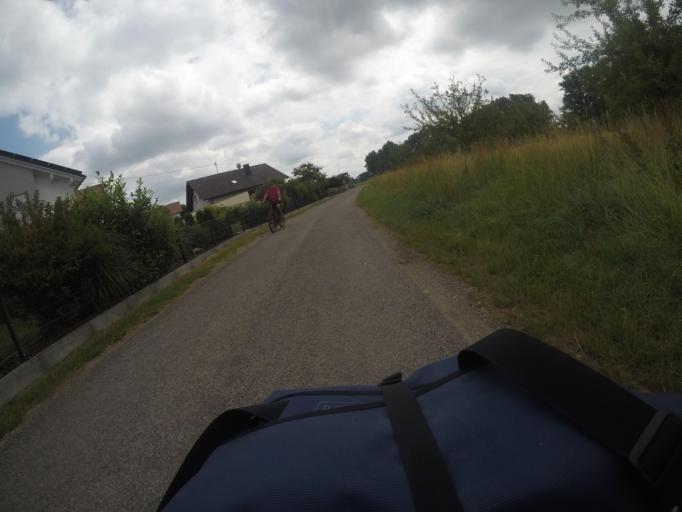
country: DE
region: Bavaria
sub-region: Swabia
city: Heimertingen
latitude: 48.0189
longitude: 10.1731
